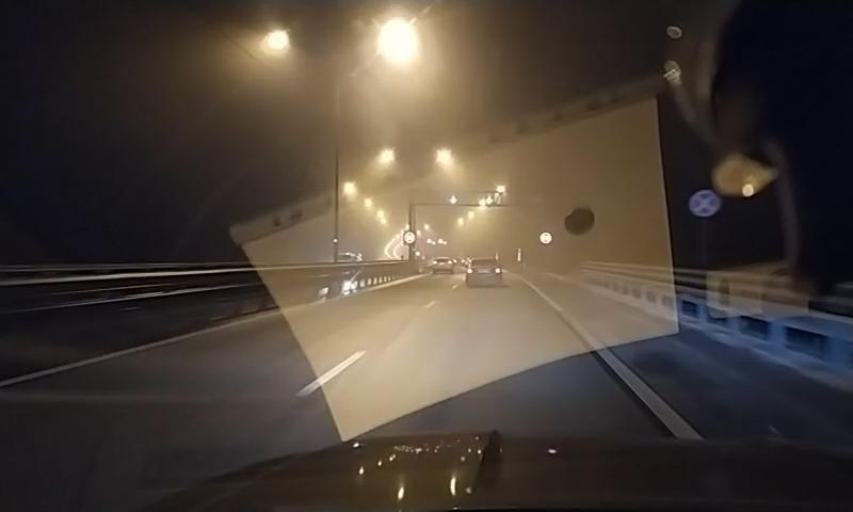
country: RU
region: Leningrad
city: Bugry
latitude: 60.1159
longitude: 30.3865
